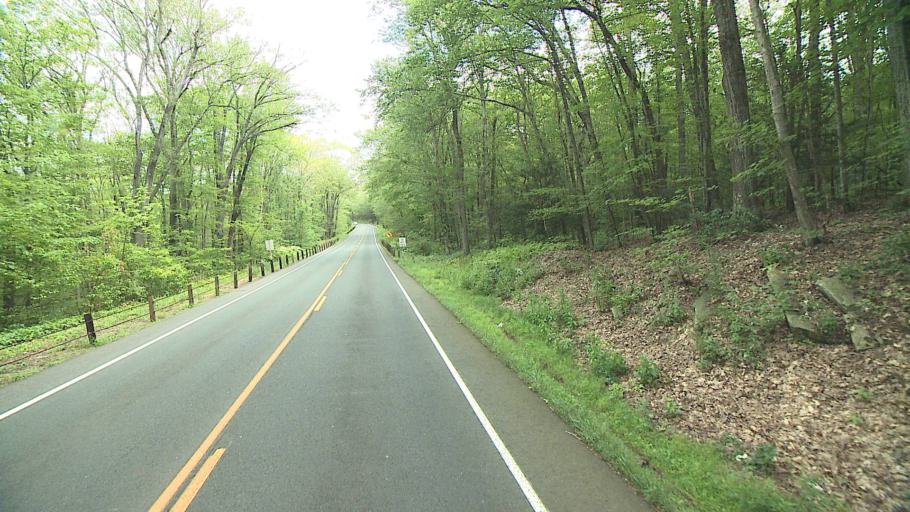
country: US
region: Connecticut
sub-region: Tolland County
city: Ellington
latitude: 41.9125
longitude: -72.4395
